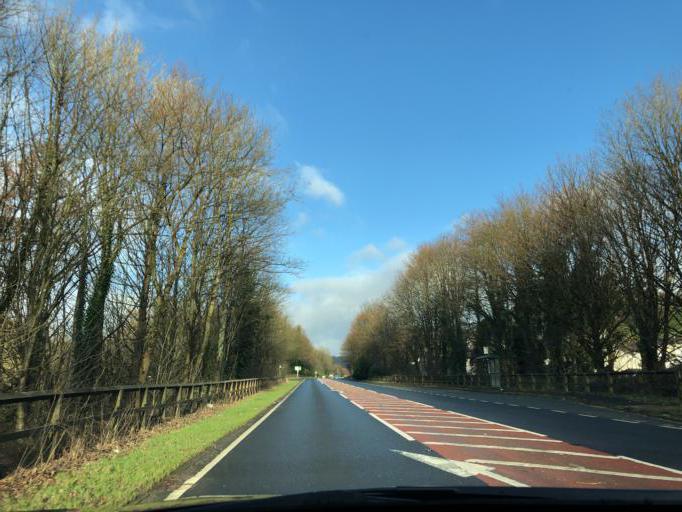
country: GB
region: England
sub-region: Cumbria
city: Grange-over-Sands
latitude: 54.2528
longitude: -2.9887
